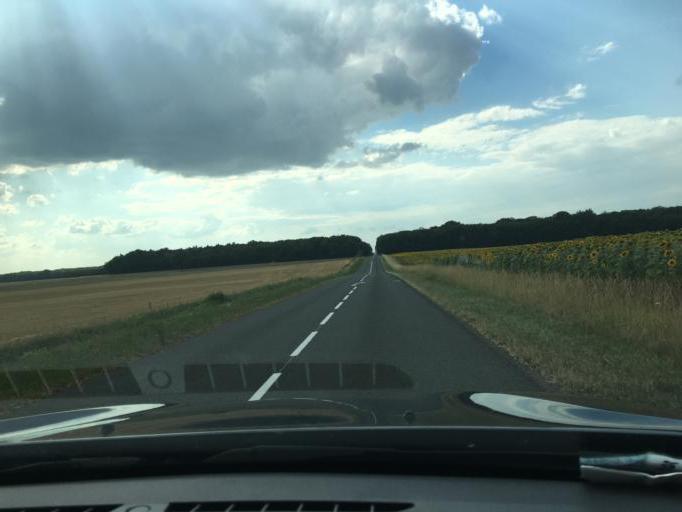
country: FR
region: Centre
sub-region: Departement du Cher
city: Baugy
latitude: 47.0999
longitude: 2.6669
